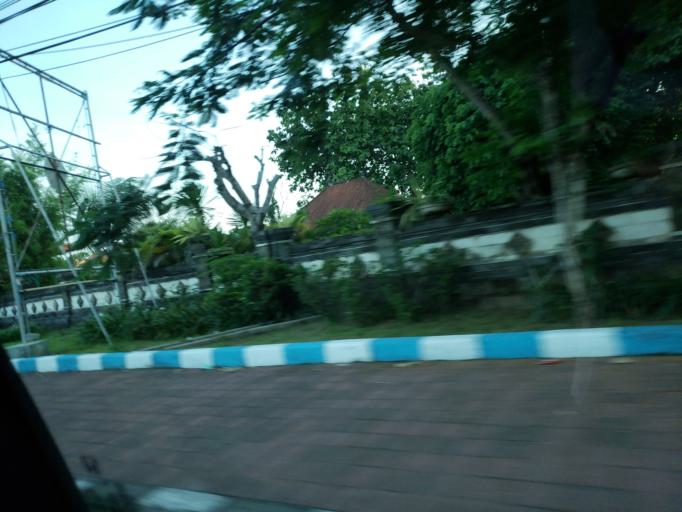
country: ID
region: Bali
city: Jimbaran
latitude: -8.7992
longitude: 115.1643
